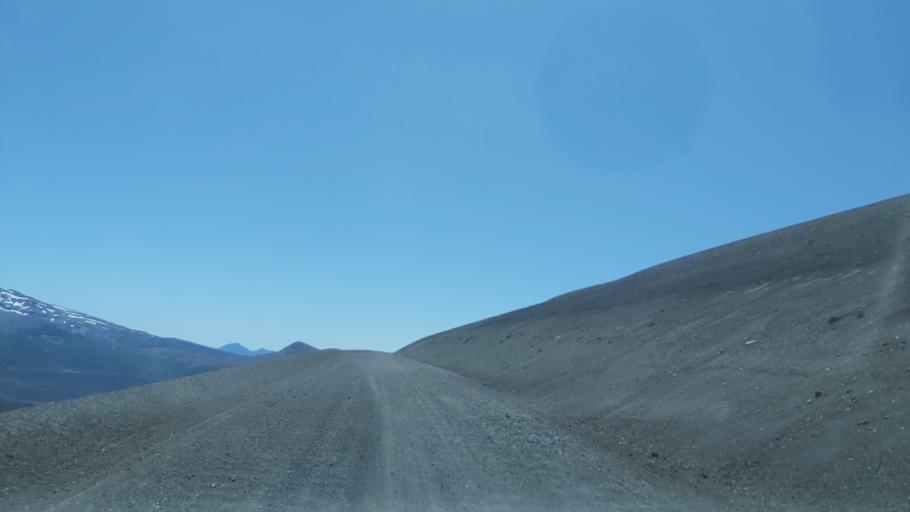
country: CL
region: Araucania
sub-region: Provincia de Cautin
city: Vilcun
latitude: -38.3710
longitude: -71.5393
